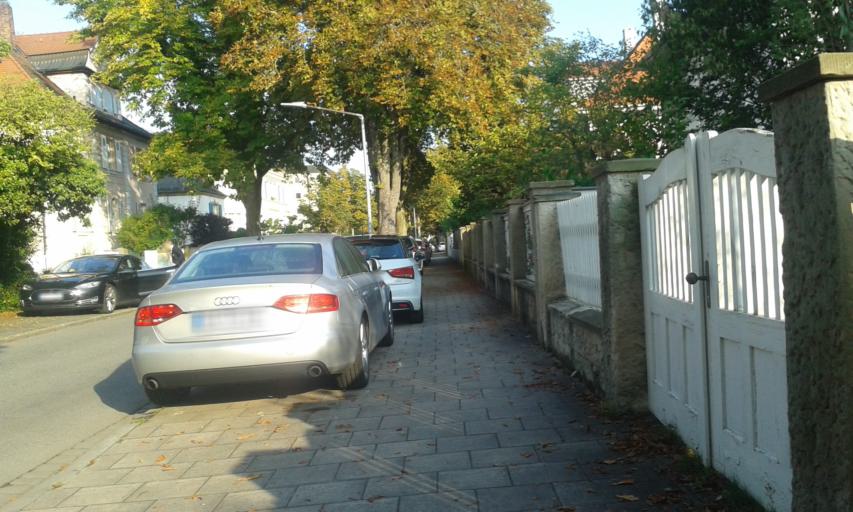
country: DE
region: Bavaria
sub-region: Upper Franconia
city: Bamberg
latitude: 49.8839
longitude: 10.8994
